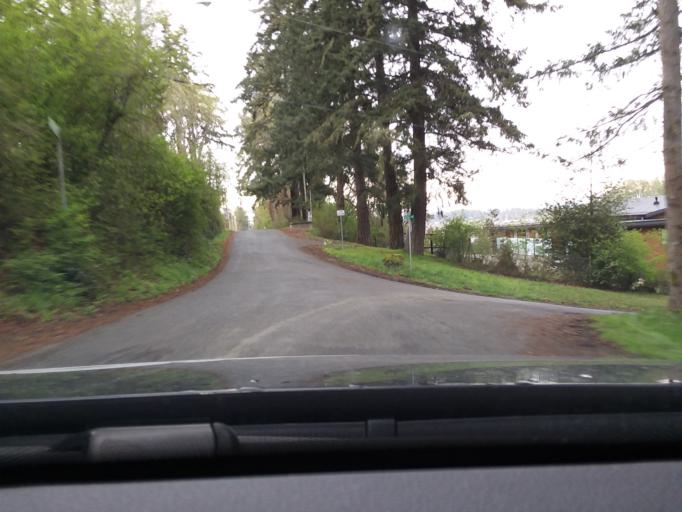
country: CA
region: British Columbia
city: Victoria
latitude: 48.5505
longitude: -123.3900
